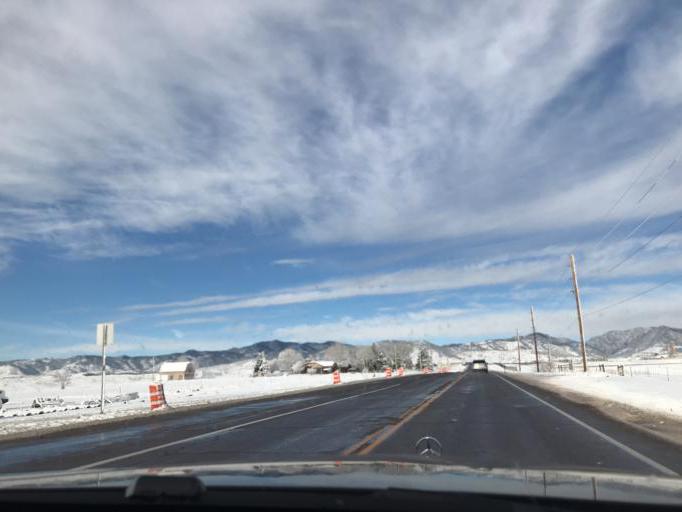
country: US
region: Colorado
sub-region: Jefferson County
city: Applewood
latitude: 39.8512
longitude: -105.1707
